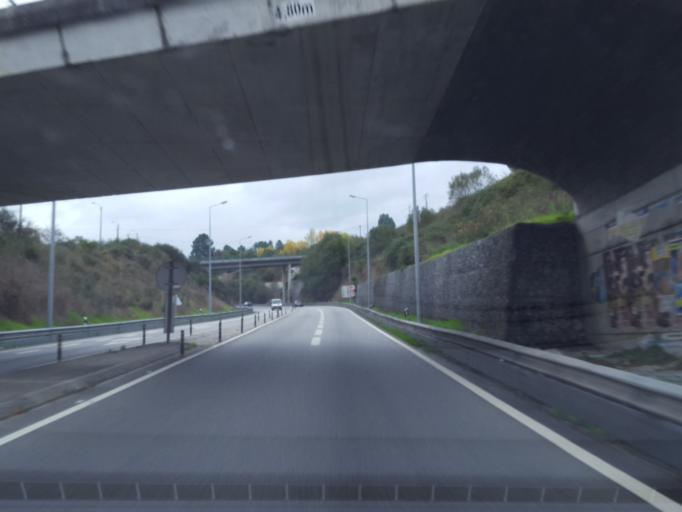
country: PT
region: Porto
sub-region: Marco de Canaveses
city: Marco de Canavezes
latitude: 41.1999
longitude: -8.1612
